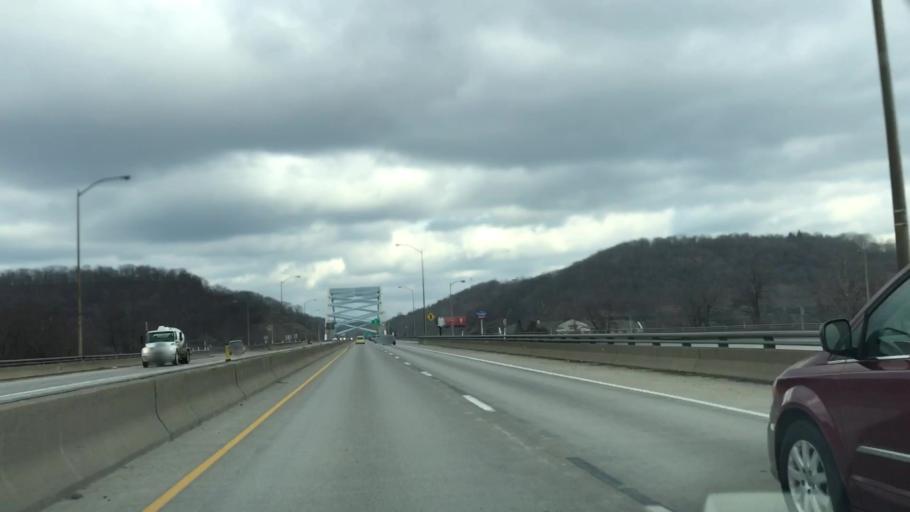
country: US
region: Pennsylvania
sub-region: Allegheny County
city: Coraopolis
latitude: 40.5103
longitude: -80.1358
